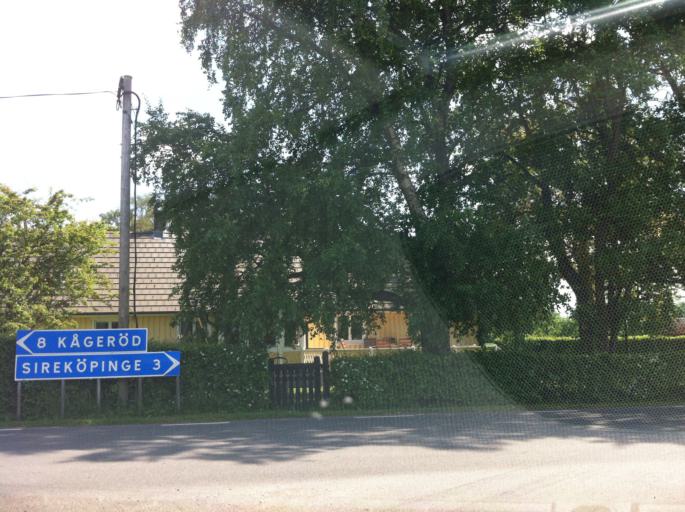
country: SE
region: Skane
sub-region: Landskrona
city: Asmundtorp
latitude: 55.9450
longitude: 12.9177
